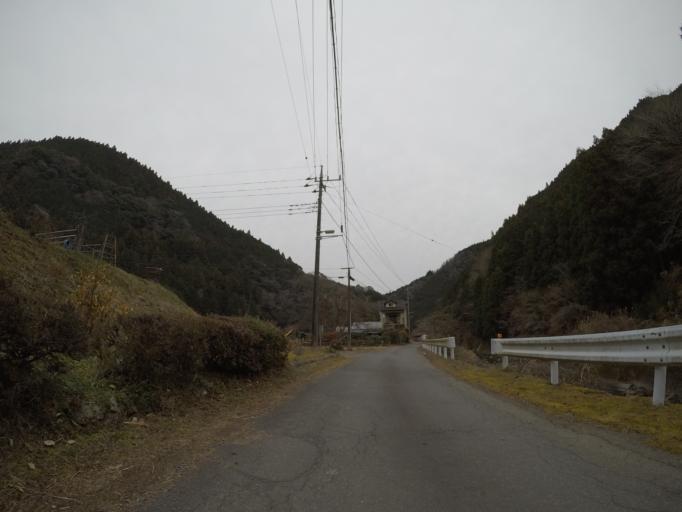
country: JP
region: Shizuoka
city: Fujinomiya
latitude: 35.2793
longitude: 138.5312
